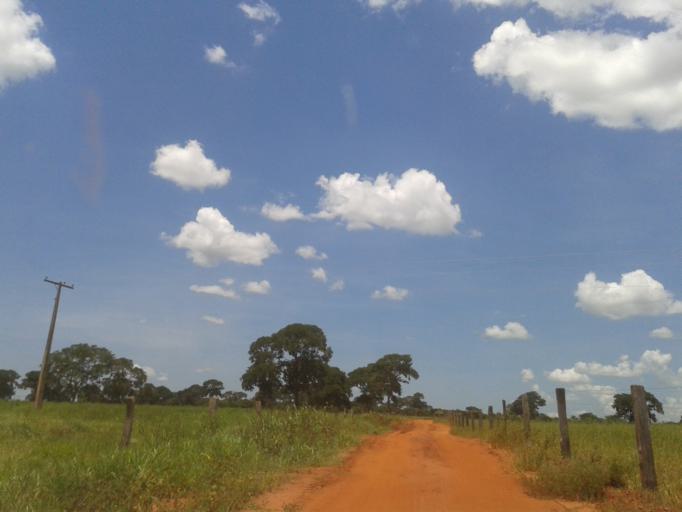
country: BR
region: Minas Gerais
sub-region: Santa Vitoria
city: Santa Vitoria
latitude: -19.2090
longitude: -50.4002
